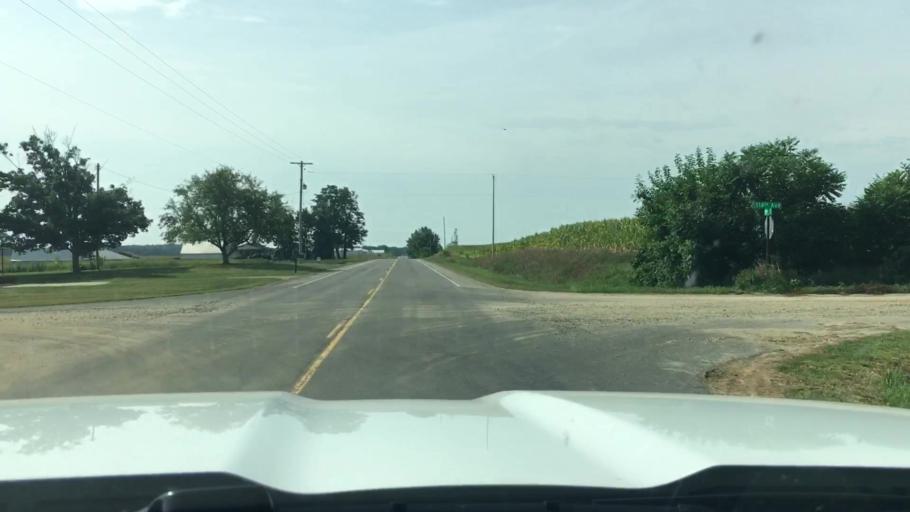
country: US
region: Michigan
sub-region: Allegan County
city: Plainwell
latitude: 42.5233
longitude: -85.6221
